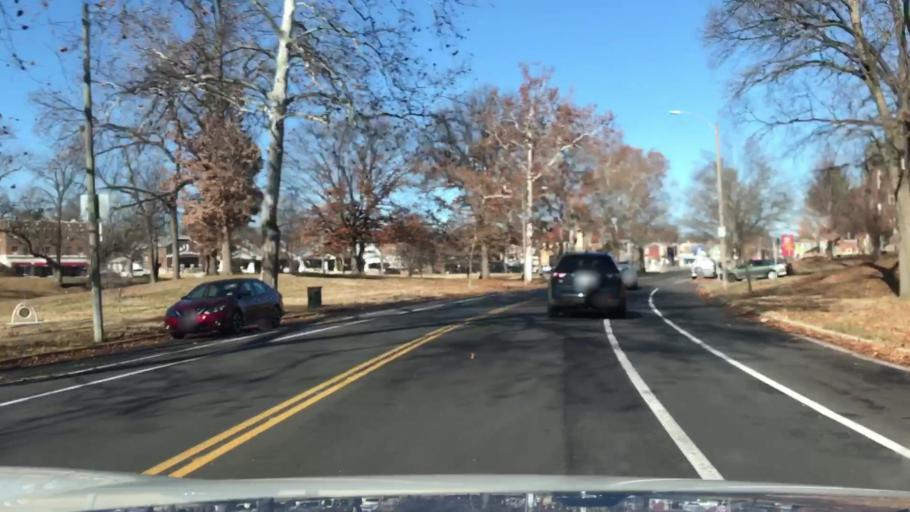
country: US
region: Missouri
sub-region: Saint Louis County
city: Lemay
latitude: 38.5822
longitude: -90.2765
